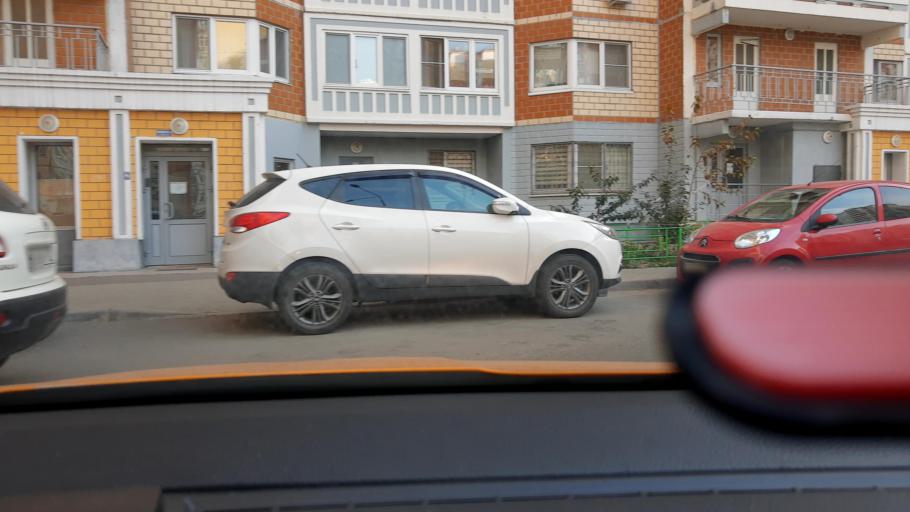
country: RU
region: Moskovskaya
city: Levoberezhnaya
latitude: 55.8708
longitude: 37.4802
